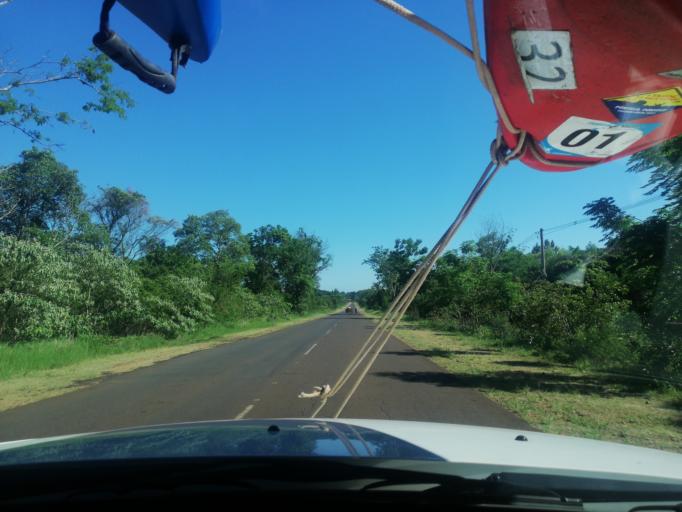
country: AR
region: Misiones
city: Santa Ana
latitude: -27.3477
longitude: -55.5836
